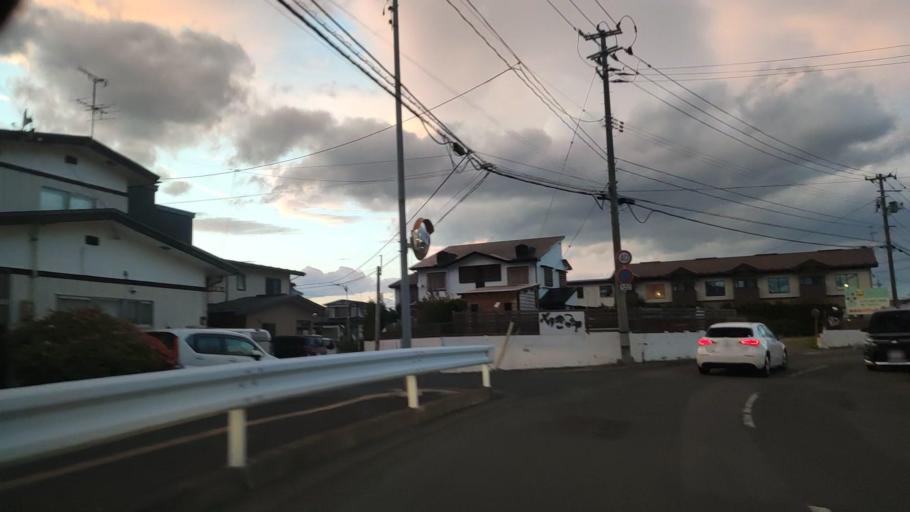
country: JP
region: Iwate
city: Morioka-shi
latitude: 39.7154
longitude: 141.1100
